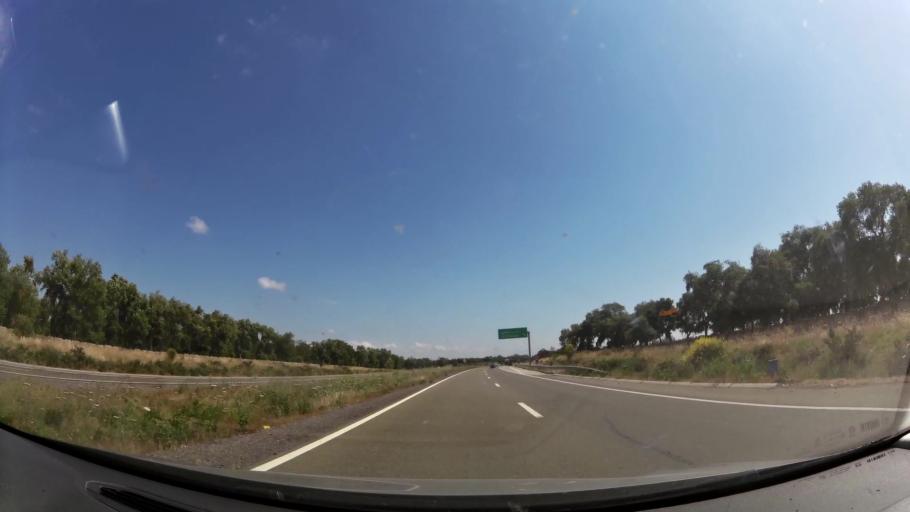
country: MA
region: Rabat-Sale-Zemmour-Zaer
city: Sale
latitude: 34.1010
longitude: -6.6846
